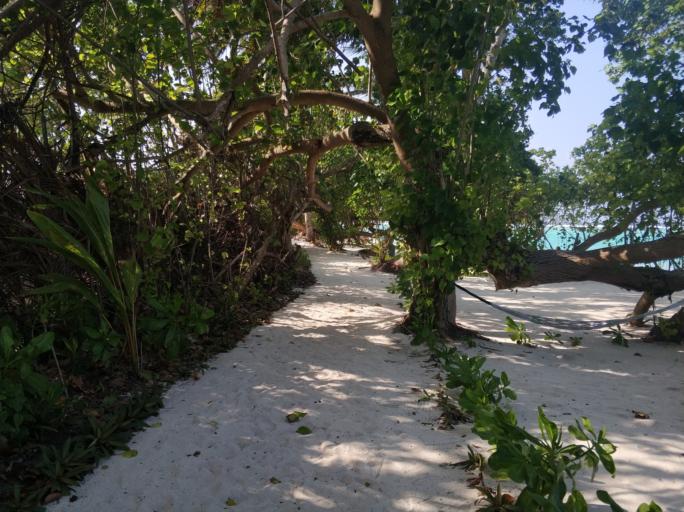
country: MV
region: Maale
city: Male
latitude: 4.4425
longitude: 72.9620
